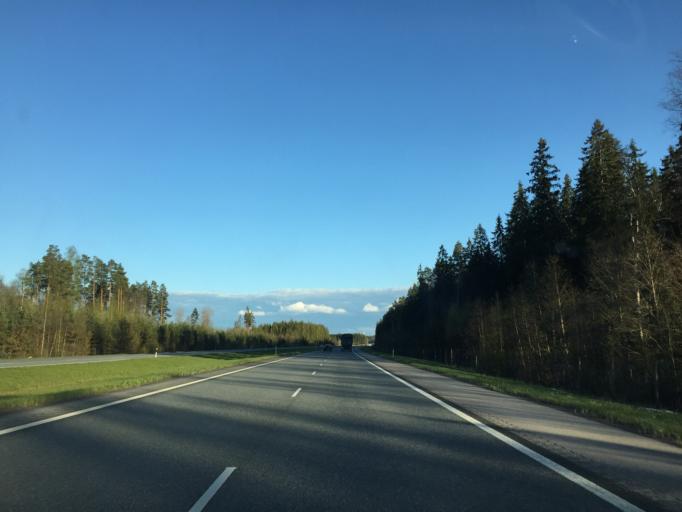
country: FI
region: Haeme
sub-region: Riihimaeki
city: Riihimaeki
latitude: 60.7797
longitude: 24.7088
